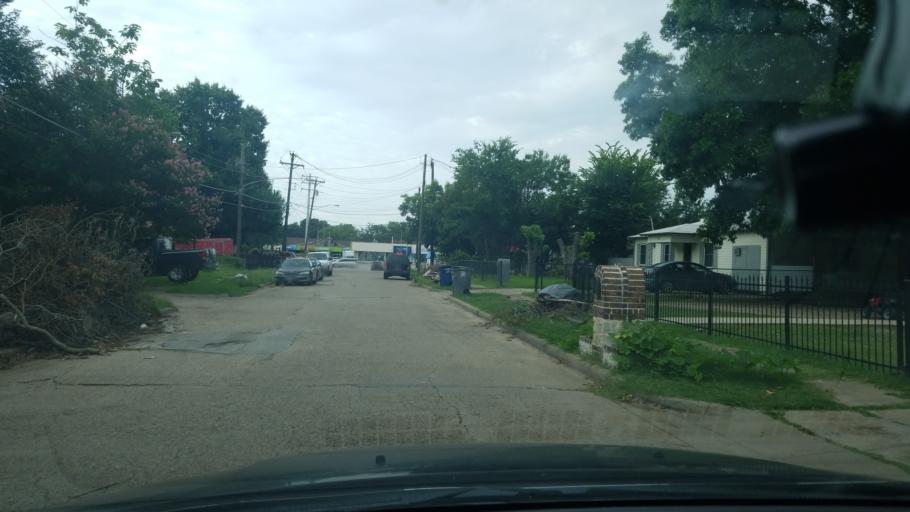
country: US
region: Texas
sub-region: Dallas County
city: Balch Springs
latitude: 32.7353
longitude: -96.6641
